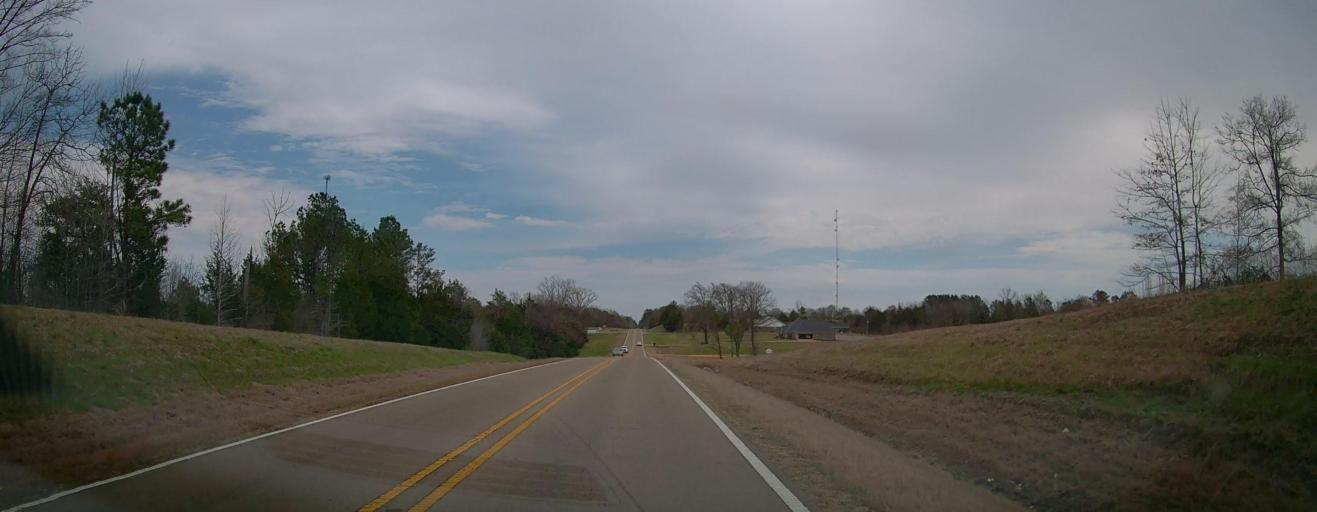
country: US
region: Mississippi
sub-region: Itawamba County
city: Mantachie
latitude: 34.2616
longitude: -88.5269
